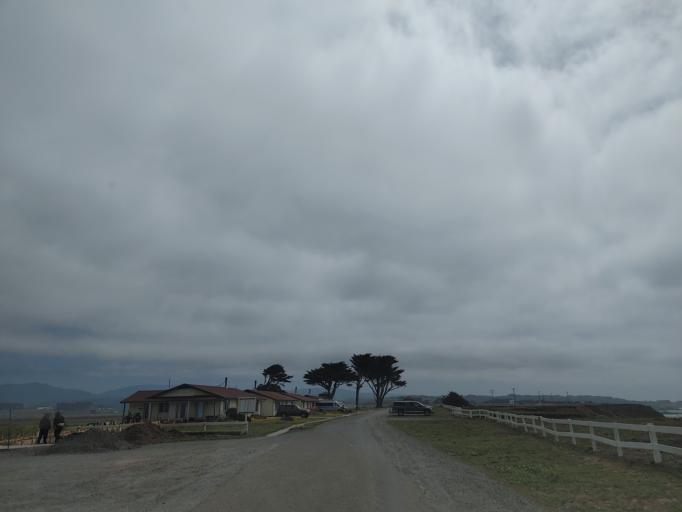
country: US
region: California
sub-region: Sonoma County
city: Sea Ranch
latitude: 38.9542
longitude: -123.7399
